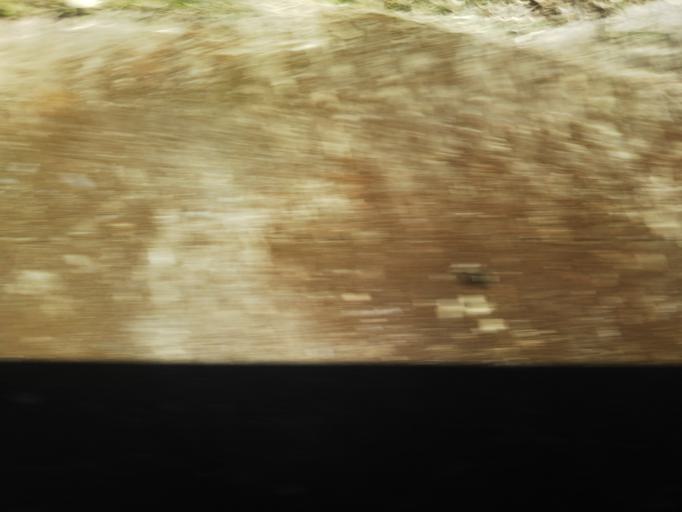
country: JP
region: Kochi
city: Nakamura
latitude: 33.0873
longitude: 133.1024
